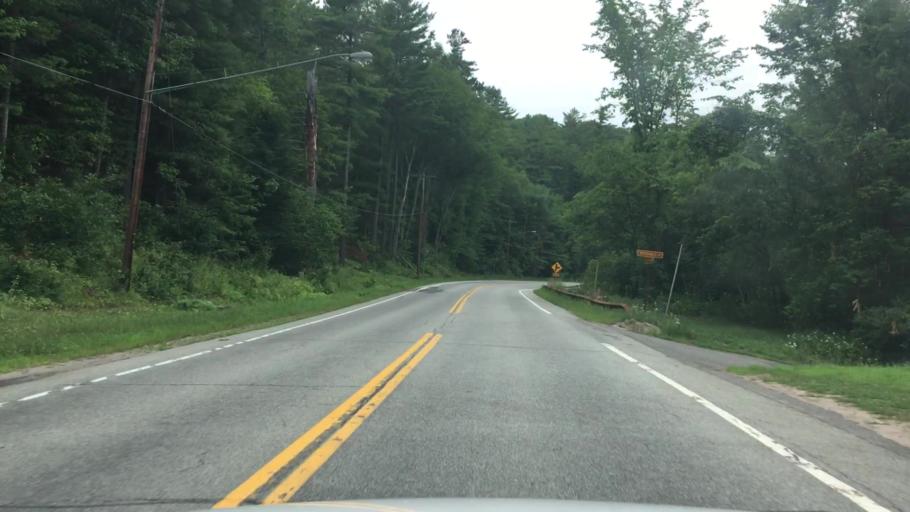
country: US
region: New York
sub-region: Clinton County
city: Peru
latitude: 44.4347
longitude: -73.6825
